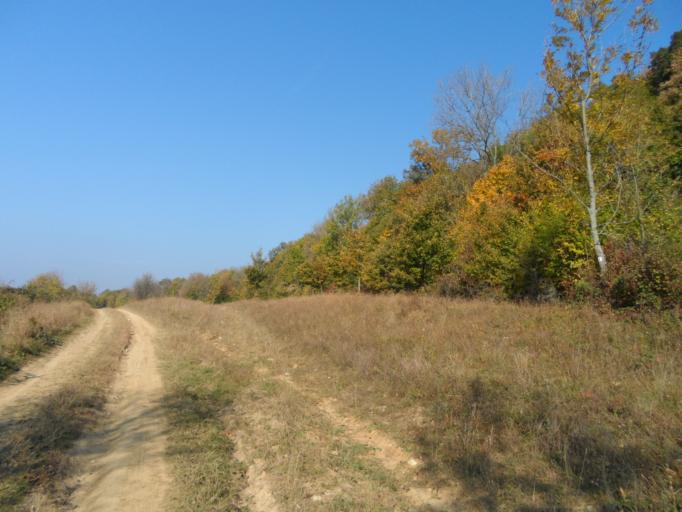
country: HU
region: Veszprem
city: Herend
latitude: 47.1755
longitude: 17.7475
